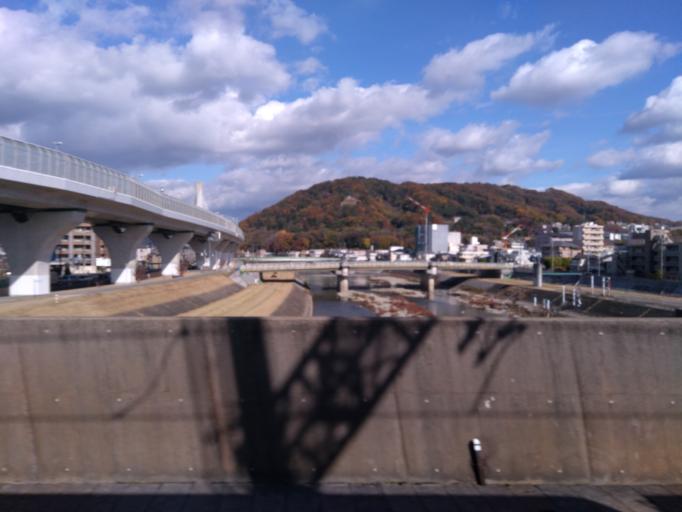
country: JP
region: Hyogo
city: Kawanishi
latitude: 34.8253
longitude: 135.4205
